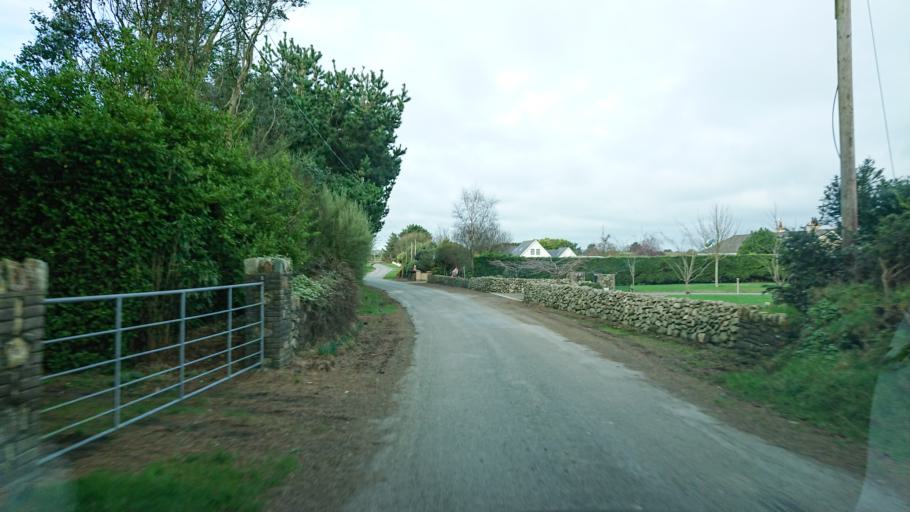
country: IE
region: Munster
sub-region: Waterford
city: Portlaw
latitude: 52.1471
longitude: -7.3073
